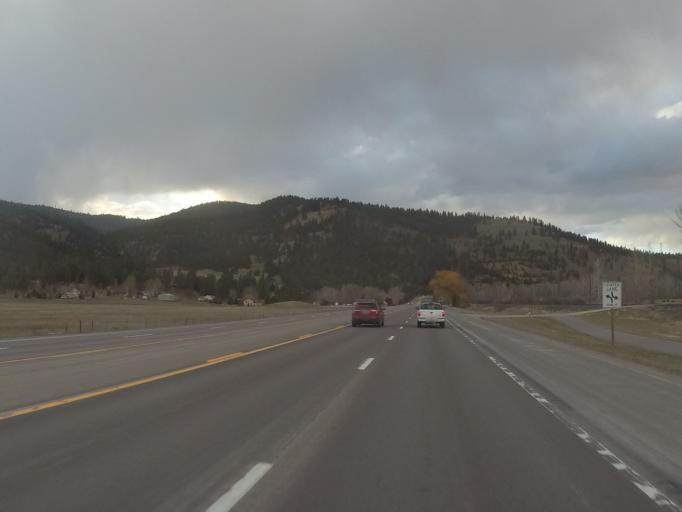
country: US
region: Montana
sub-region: Missoula County
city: Lolo
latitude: 46.7822
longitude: -114.0942
